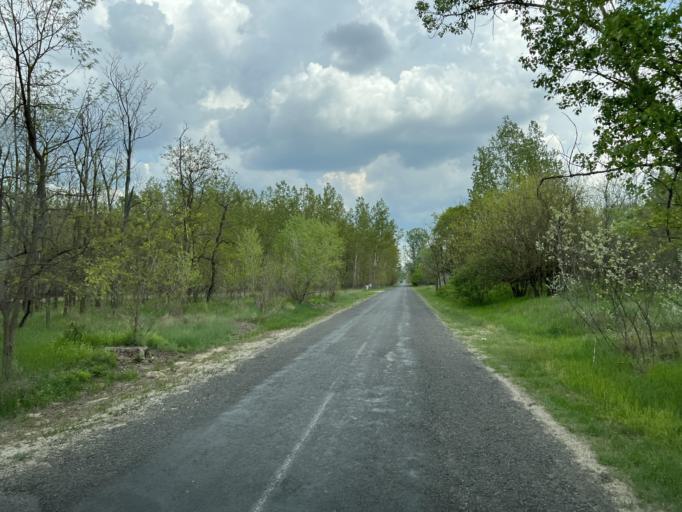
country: HU
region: Pest
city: Csemo
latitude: 47.0981
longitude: 19.7418
